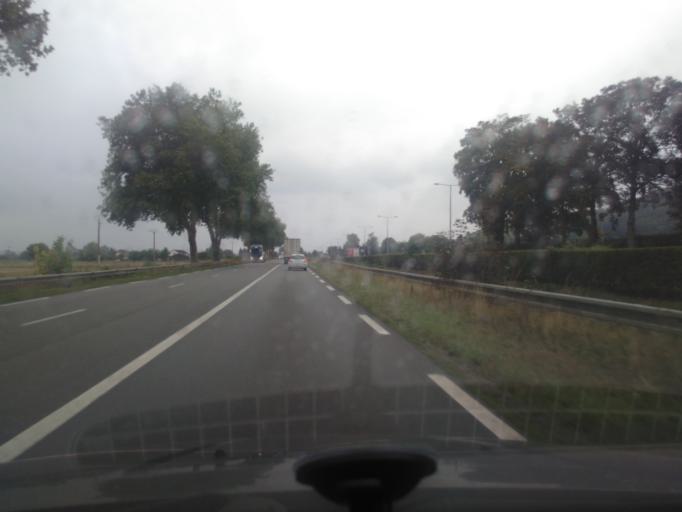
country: FR
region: Picardie
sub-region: Departement de l'Aisne
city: Laon
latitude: 49.5578
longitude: 3.6352
